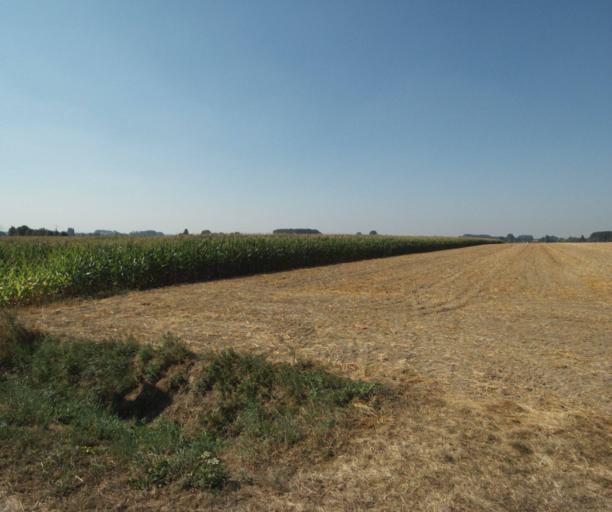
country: FR
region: Nord-Pas-de-Calais
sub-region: Departement du Nord
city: Wervicq-Sud
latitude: 50.7543
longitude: 3.0516
